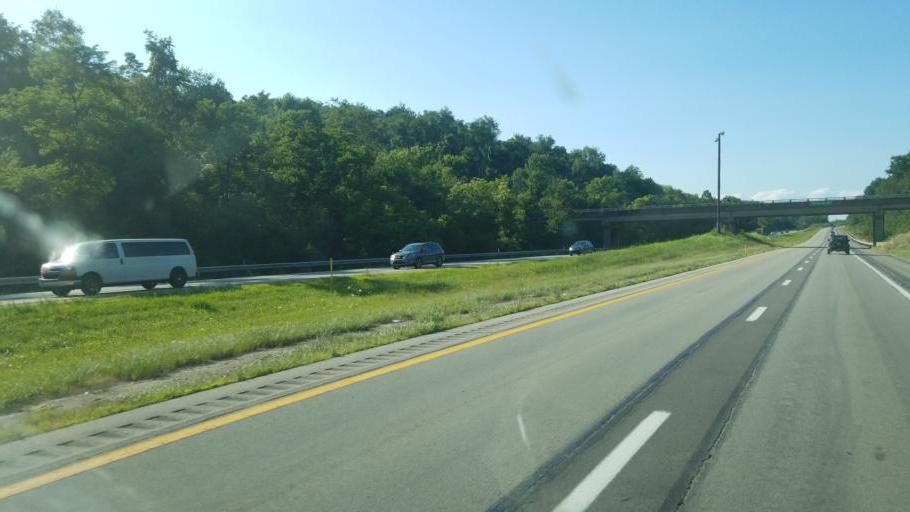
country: US
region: Pennsylvania
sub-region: Washington County
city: East Washington
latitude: 40.0528
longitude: -80.1848
